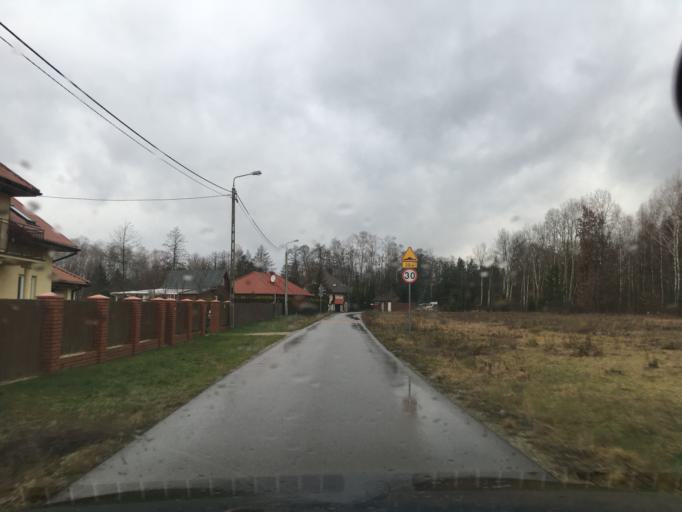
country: PL
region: Masovian Voivodeship
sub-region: Powiat piaseczynski
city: Lesznowola
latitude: 52.0608
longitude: 20.9262
